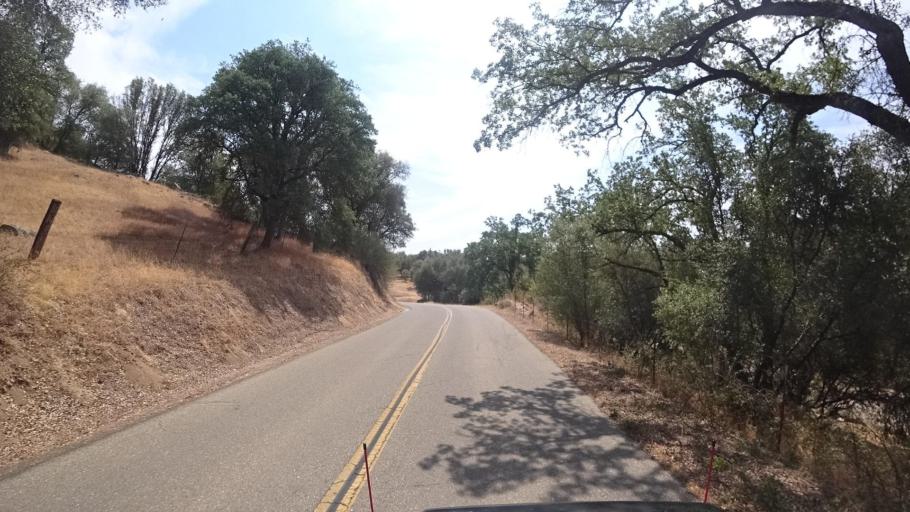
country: US
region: California
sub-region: Mariposa County
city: Mariposa
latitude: 37.4147
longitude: -119.8603
